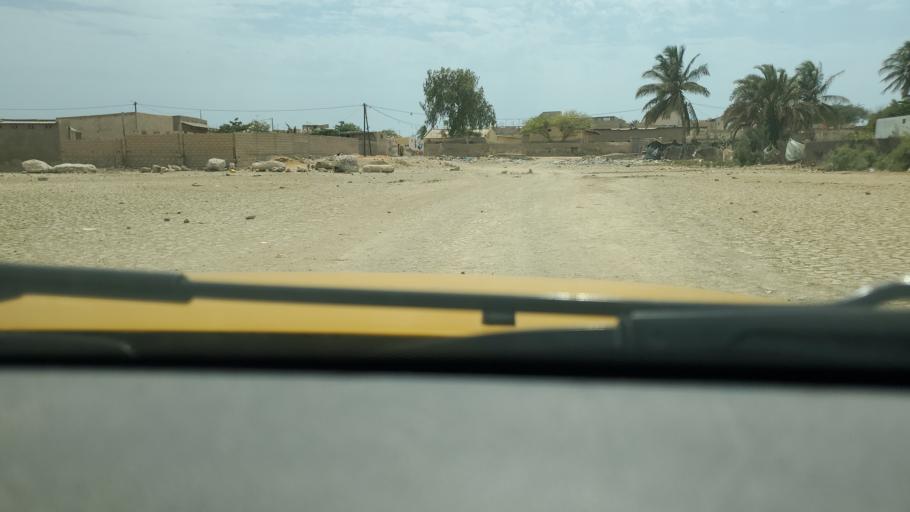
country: SN
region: Saint-Louis
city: Saint-Louis
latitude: 16.0255
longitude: -16.4729
